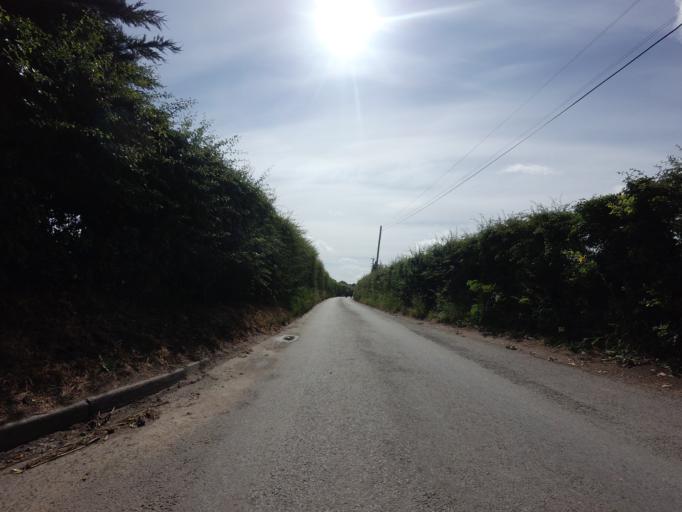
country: GB
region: England
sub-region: Greater London
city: Orpington
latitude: 51.3780
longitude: 0.1356
